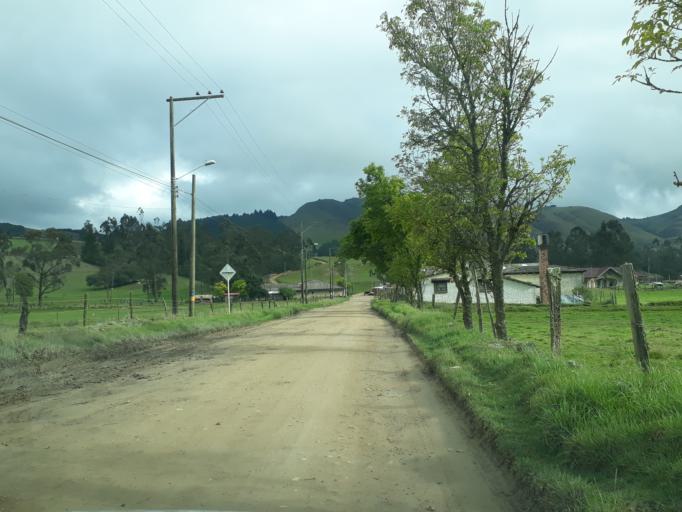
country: CO
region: Cundinamarca
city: Cucunuba
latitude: 5.1937
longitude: -73.7528
